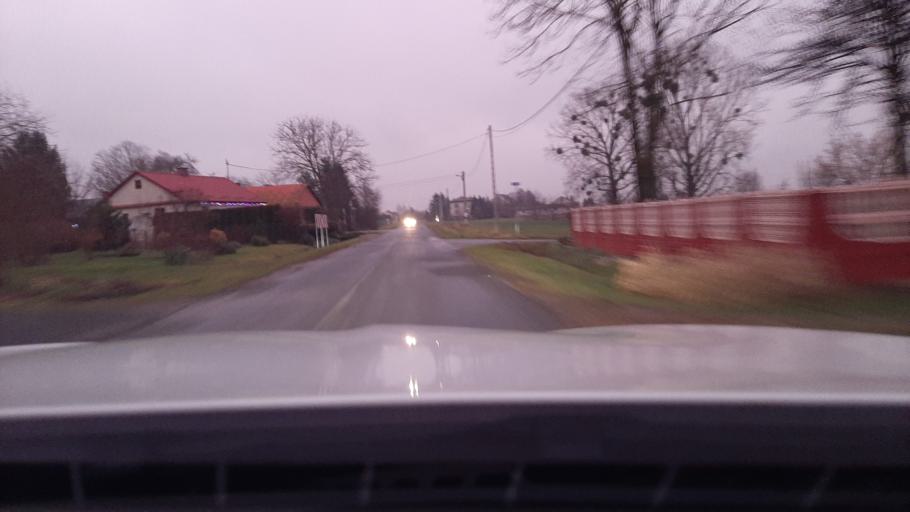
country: PL
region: Lublin Voivodeship
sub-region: Powiat lubelski
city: Garbow
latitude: 51.3530
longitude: 22.3933
